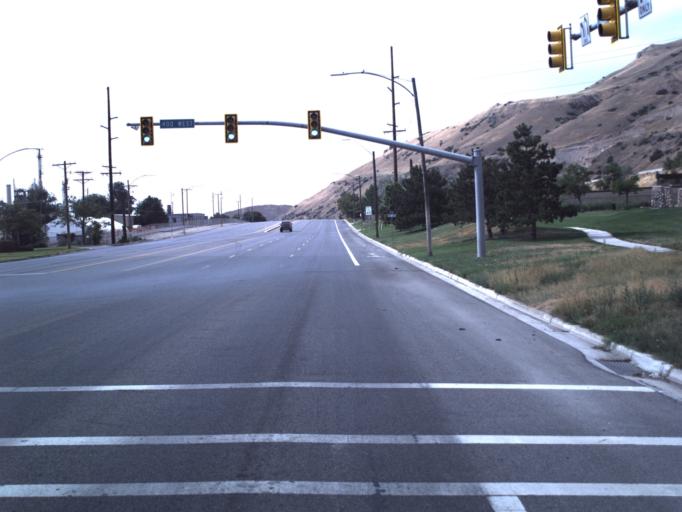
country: US
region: Utah
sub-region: Salt Lake County
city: Salt Lake City
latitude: 40.7900
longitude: -111.9008
